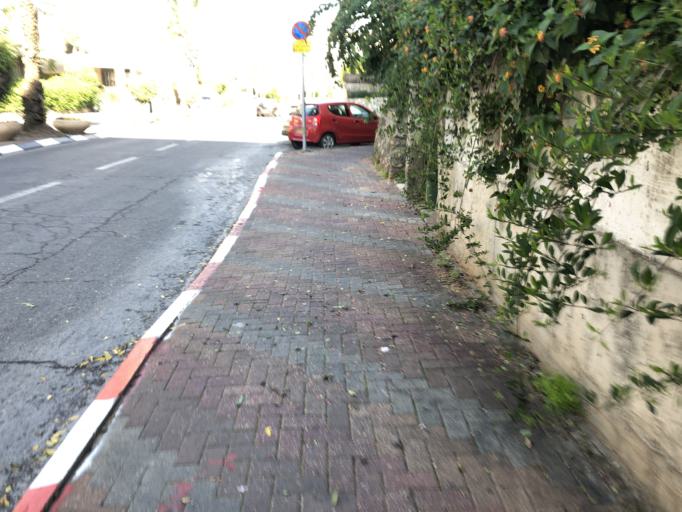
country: IL
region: Tel Aviv
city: Ramat Gan
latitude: 32.0814
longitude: 34.8204
